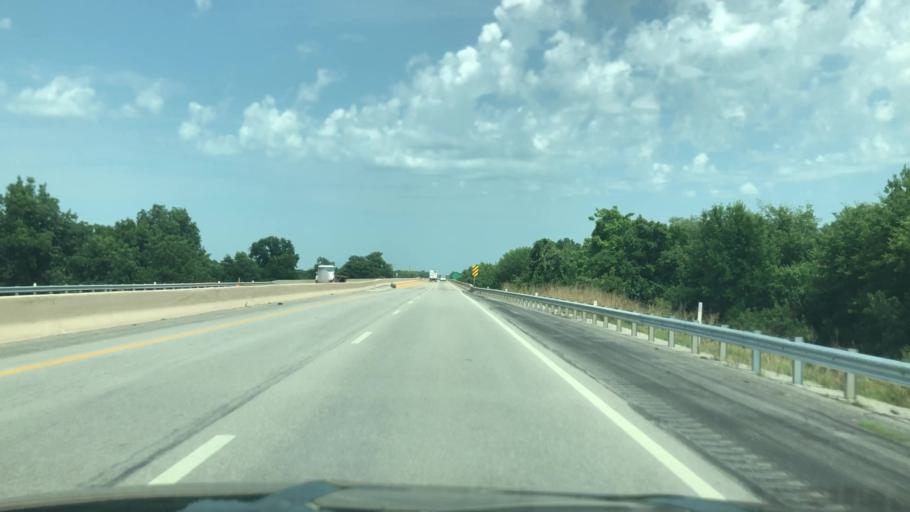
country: US
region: Oklahoma
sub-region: Rogers County
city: Verdigris
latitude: 36.2091
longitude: -95.7008
